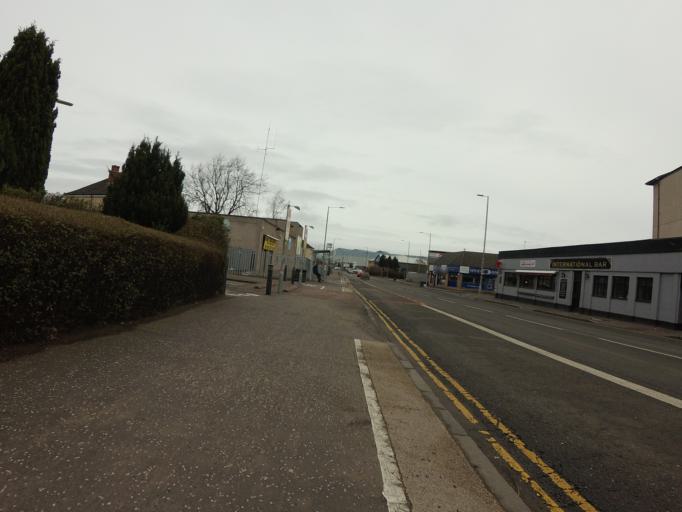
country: GB
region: Scotland
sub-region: Glasgow City
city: Glasgow
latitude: 55.8344
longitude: -4.2488
